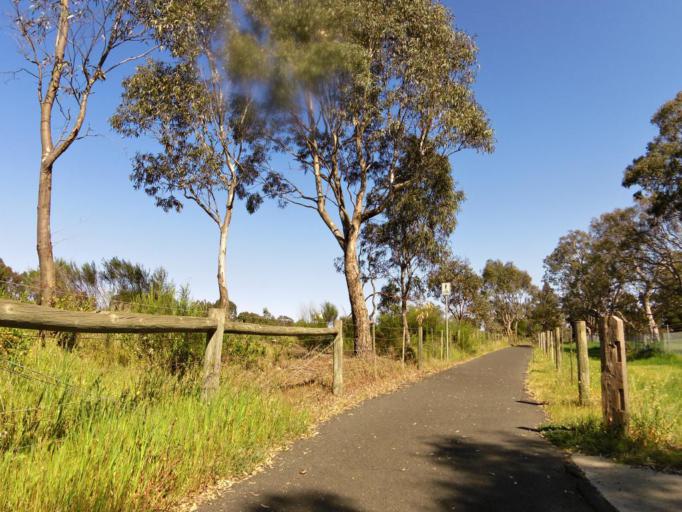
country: AU
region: Victoria
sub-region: Banyule
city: Bundoora
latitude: -37.6865
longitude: 145.0722
